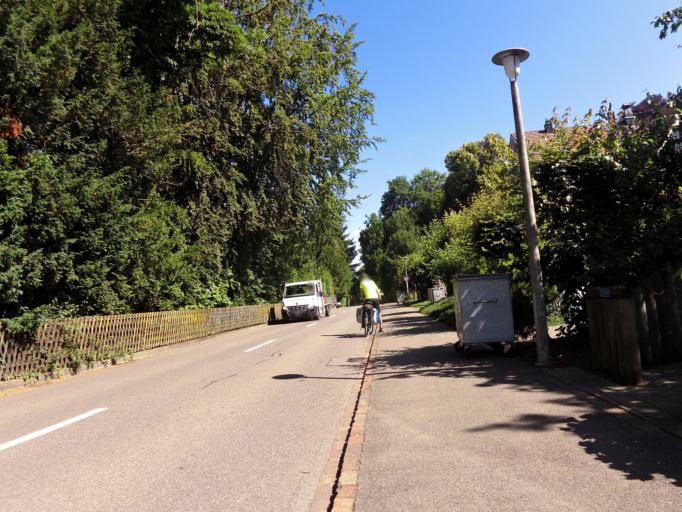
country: CH
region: Thurgau
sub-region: Kreuzlingen District
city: Gottlieben
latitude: 47.6603
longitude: 9.1347
